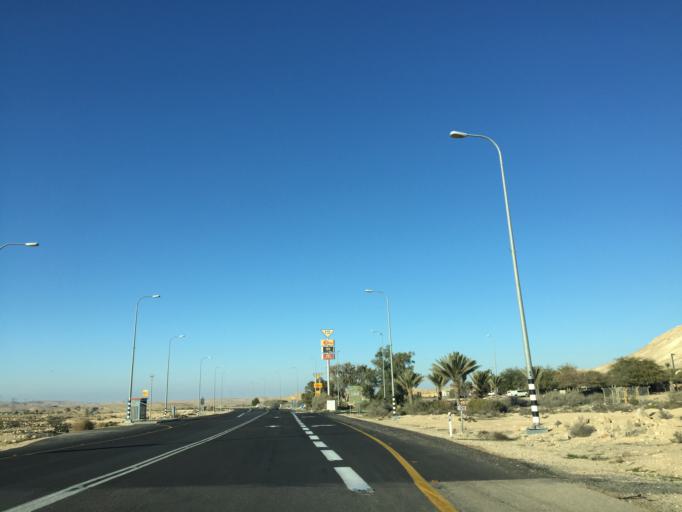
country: IL
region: Southern District
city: Midreshet Ben-Gurion
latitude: 30.7905
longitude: 34.7679
